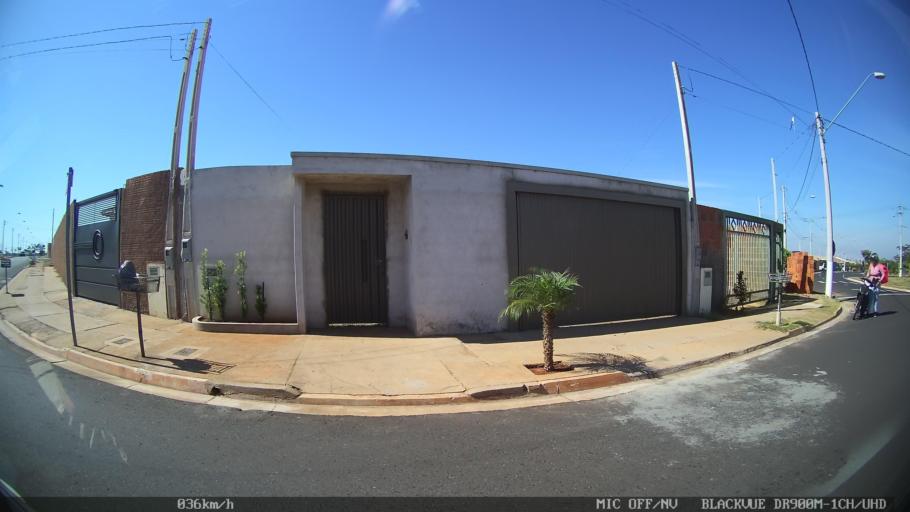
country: BR
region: Sao Paulo
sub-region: Sao Jose Do Rio Preto
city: Sao Jose do Rio Preto
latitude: -20.7487
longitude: -49.4378
